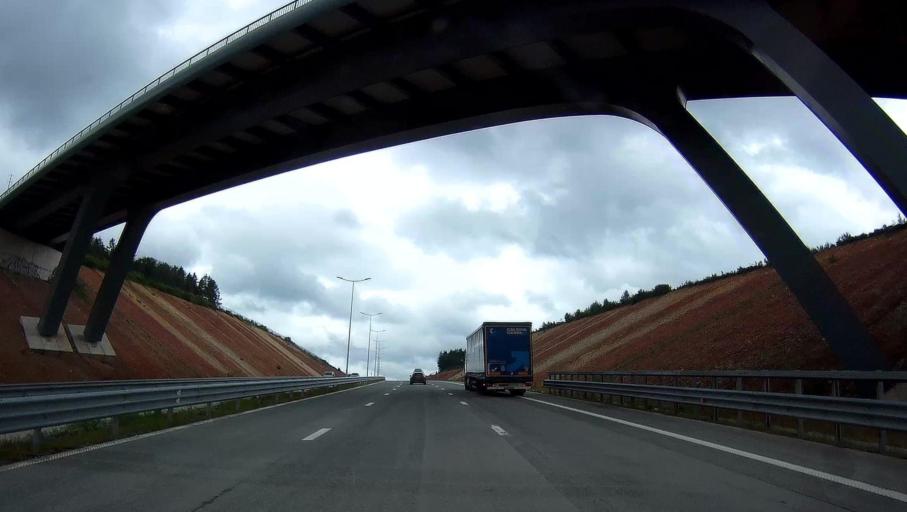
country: BE
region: Wallonia
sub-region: Province de Namur
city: Couvin
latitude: 50.0285
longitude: 4.5130
